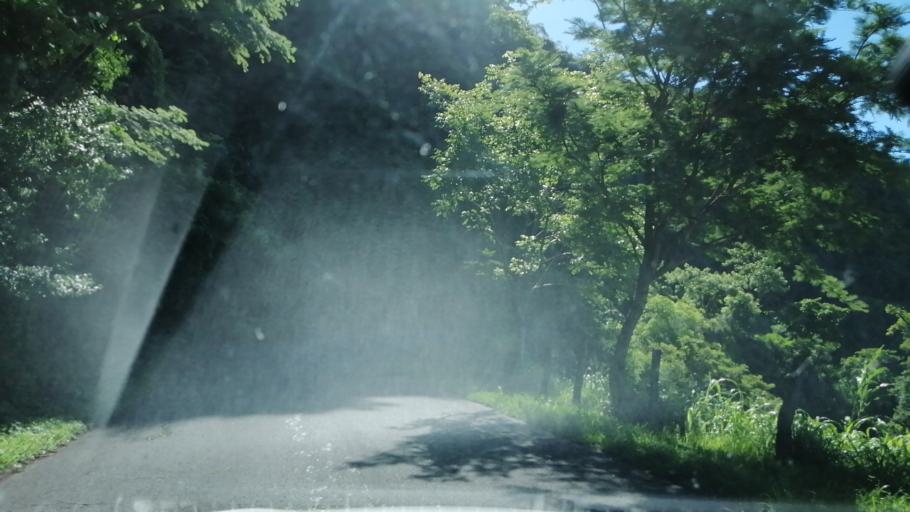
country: SV
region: Morazan
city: Corinto
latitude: 13.7905
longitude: -88.0169
